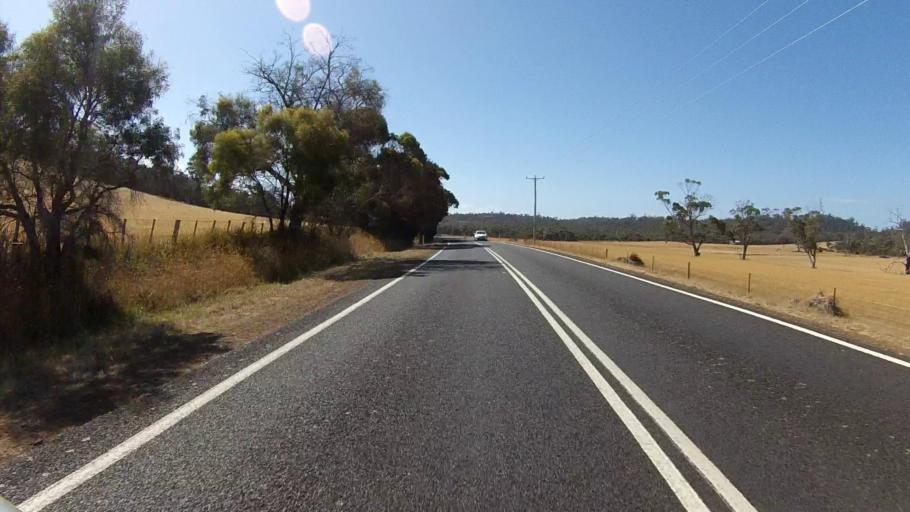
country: AU
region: Tasmania
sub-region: Sorell
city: Sorell
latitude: -42.4223
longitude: 147.9344
